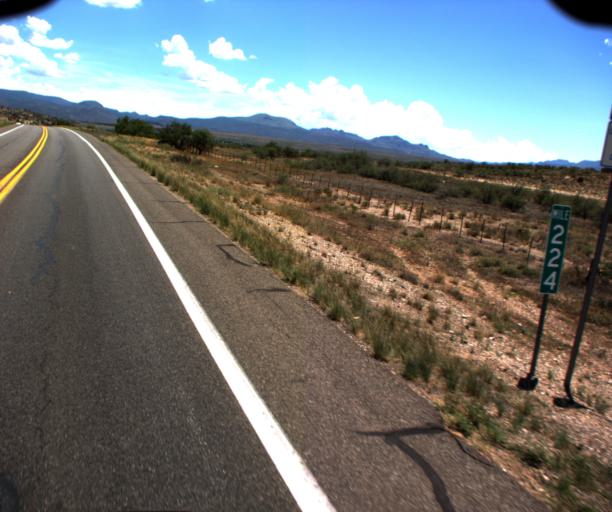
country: US
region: Arizona
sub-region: Yavapai County
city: Camp Verde
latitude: 34.5357
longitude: -111.8170
